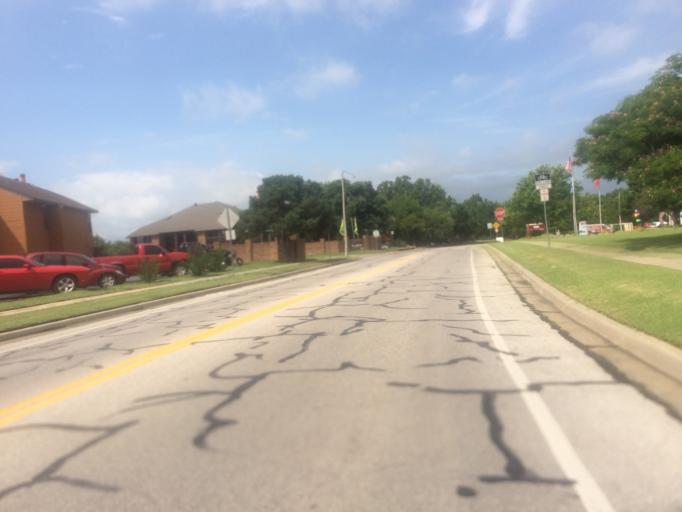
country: US
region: Oklahoma
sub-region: Cleveland County
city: Norman
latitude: 35.1827
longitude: -97.4239
